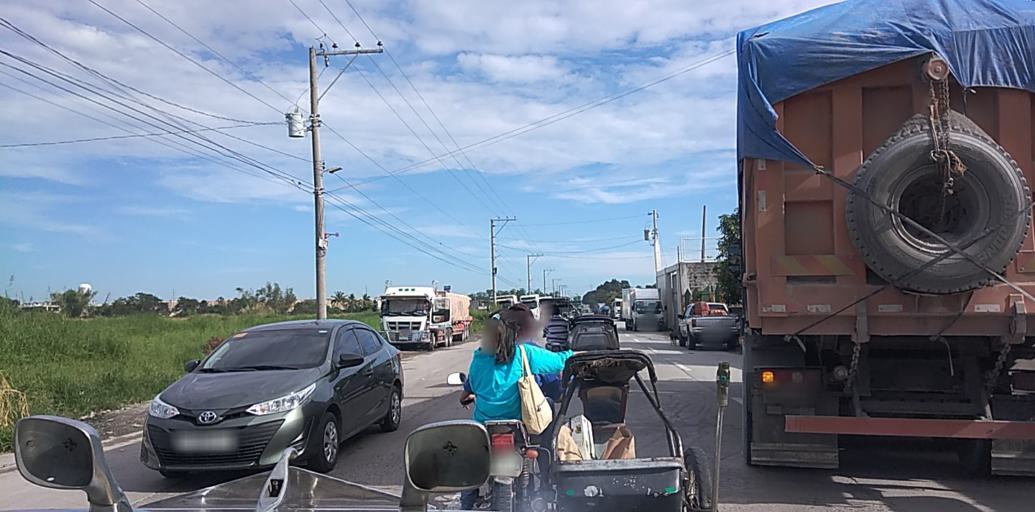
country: PH
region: Central Luzon
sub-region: Province of Pampanga
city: Bulaon
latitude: 15.1023
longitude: 120.6587
